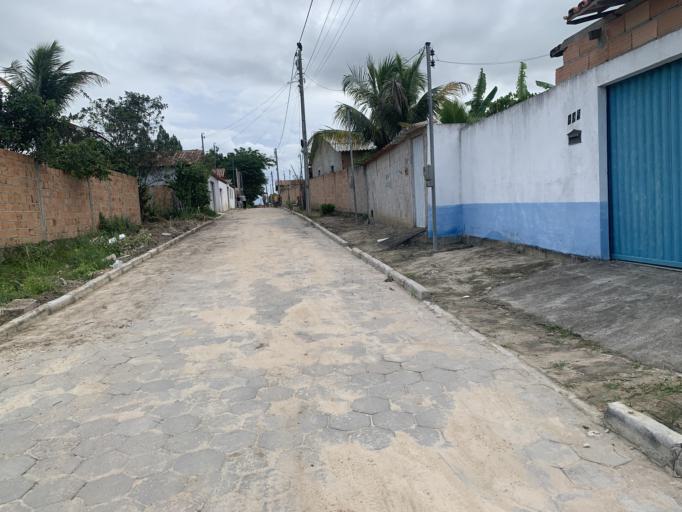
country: BR
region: Bahia
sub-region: Medeiros Neto
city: Medeiros Neto
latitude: -17.3903
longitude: -40.2327
